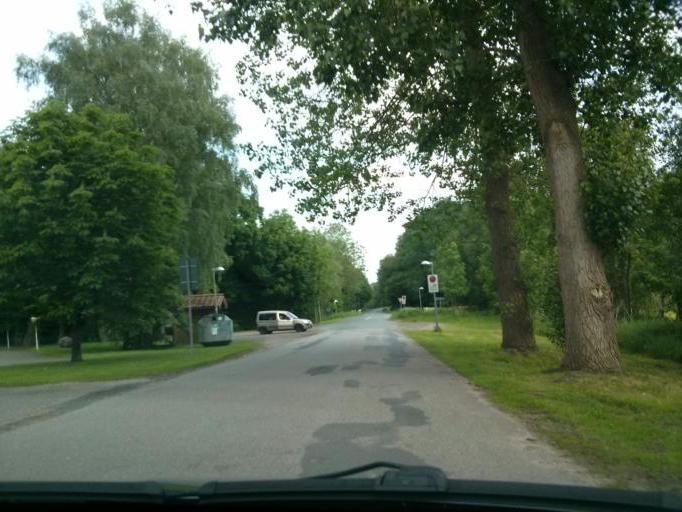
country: DE
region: Lower Saxony
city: Loxstedt
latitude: 53.4954
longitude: 8.6368
